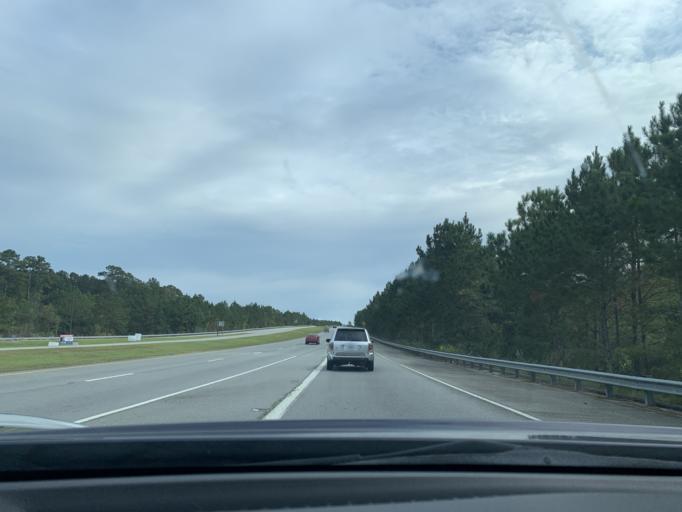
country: US
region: Georgia
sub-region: Chatham County
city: Pooler
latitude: 32.1155
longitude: -81.2689
